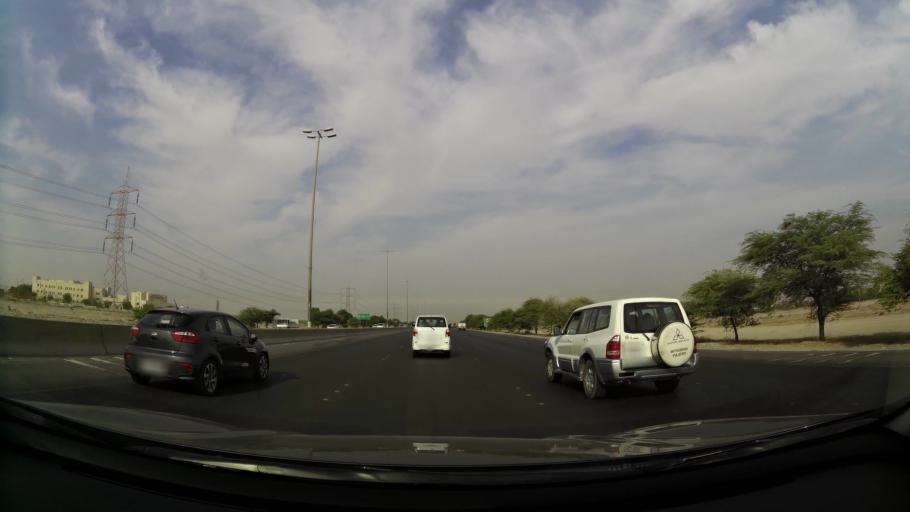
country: KW
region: Al Asimah
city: Ar Rabiyah
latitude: 29.2680
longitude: 47.8277
